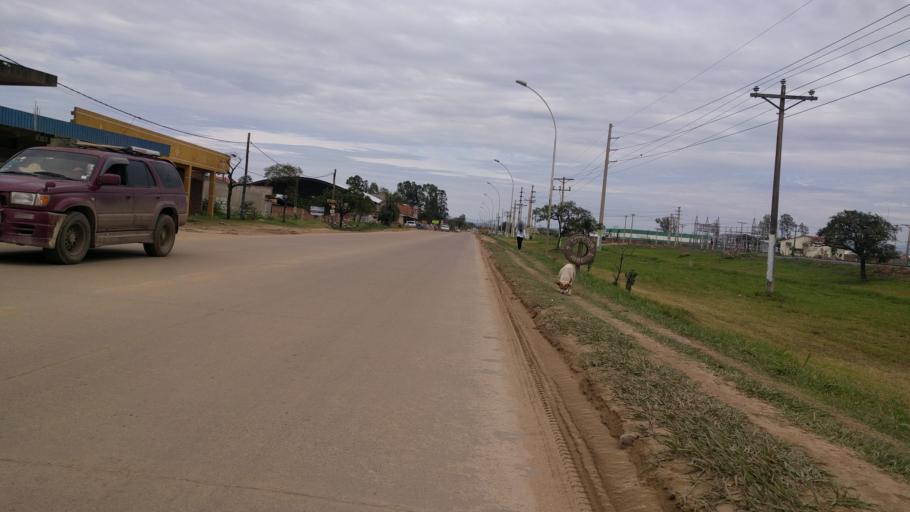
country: BO
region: Santa Cruz
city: Santa Cruz de la Sierra
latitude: -17.8471
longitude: -63.1767
